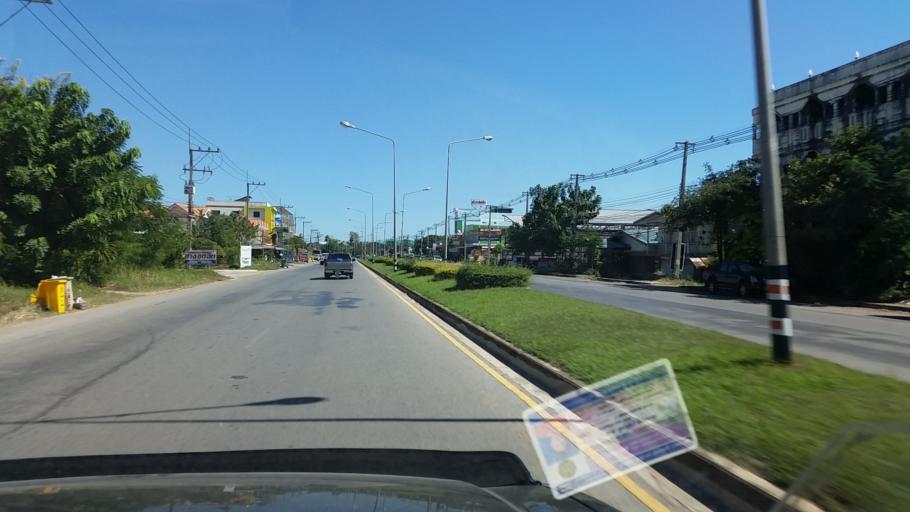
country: TH
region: Chaiyaphum
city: Chaiyaphum
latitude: 15.7961
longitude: 102.0181
